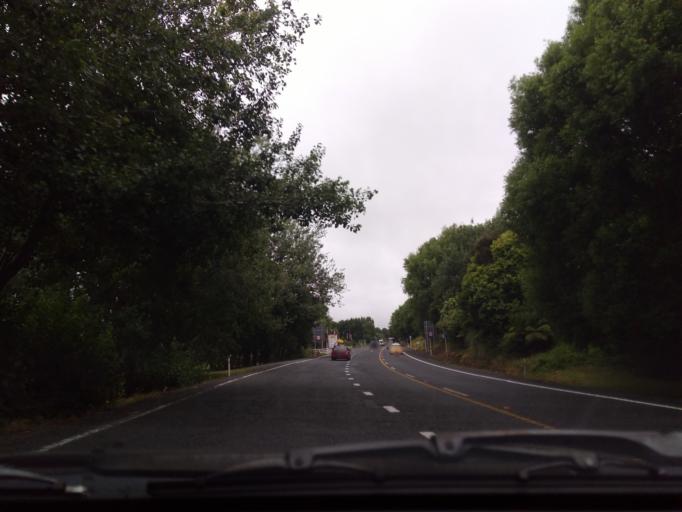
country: NZ
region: Auckland
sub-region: Auckland
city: Wellsford
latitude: -36.1595
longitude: 174.4422
